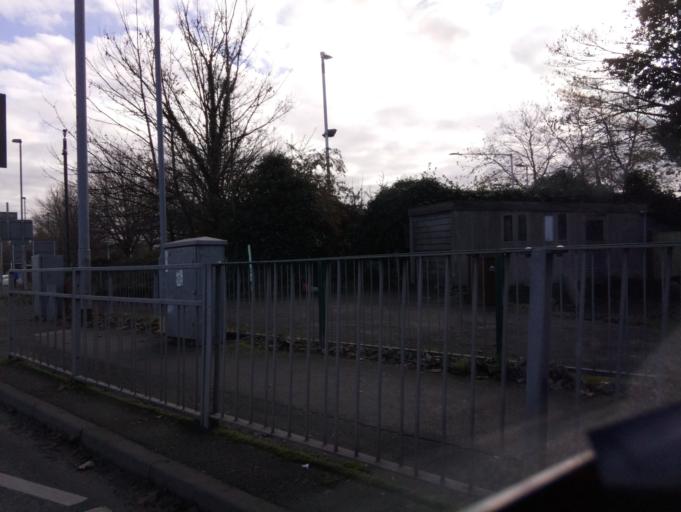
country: GB
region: England
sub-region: Staffordshire
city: Burton upon Trent
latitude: 52.7978
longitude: -1.6356
